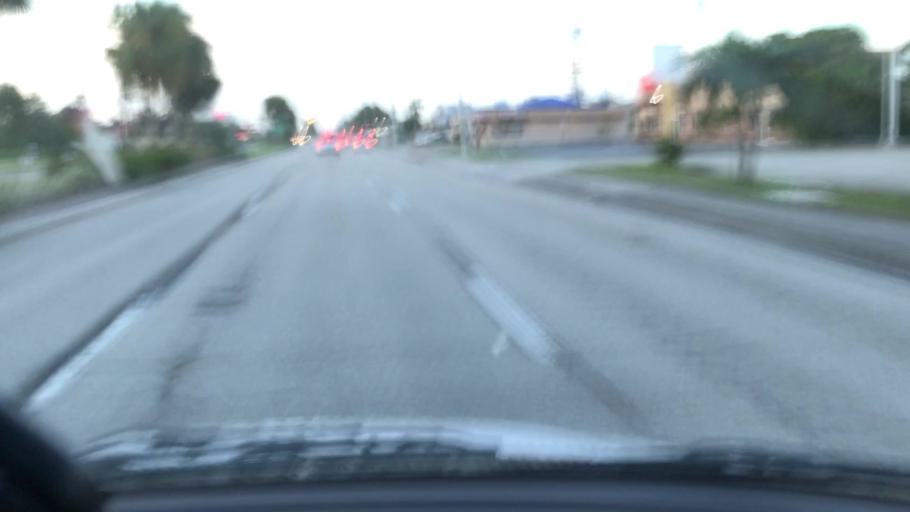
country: US
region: Florida
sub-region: Lee County
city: Cape Coral
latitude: 26.5911
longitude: -81.9419
